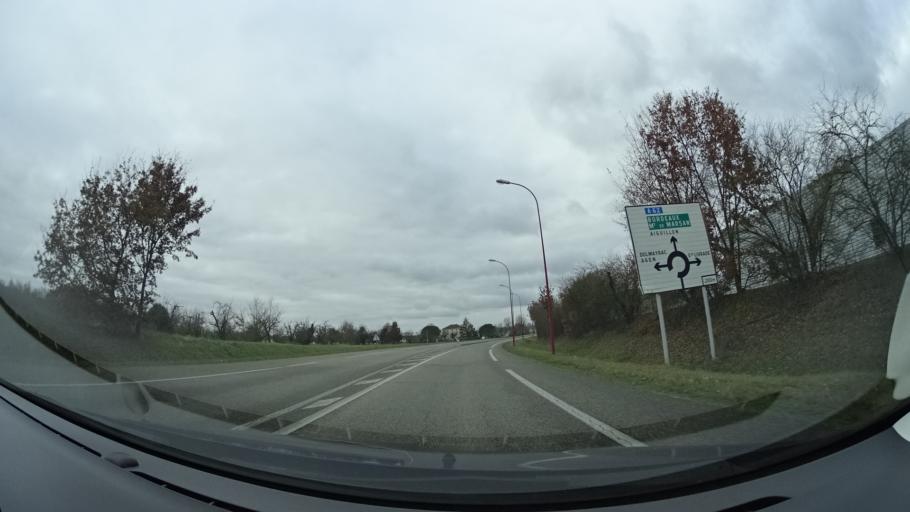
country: FR
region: Aquitaine
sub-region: Departement du Lot-et-Garonne
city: Sainte-Livrade-sur-Lot
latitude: 44.3875
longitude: 0.5859
